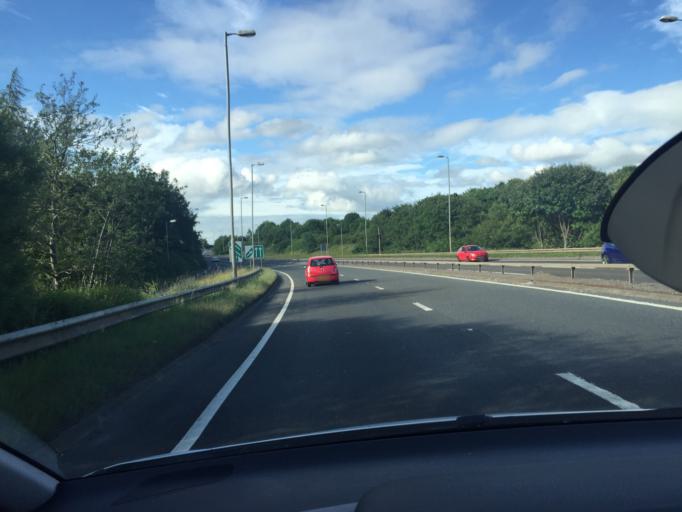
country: GB
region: Scotland
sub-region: South Lanarkshire
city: High Blantyre
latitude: 55.7853
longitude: -4.0874
